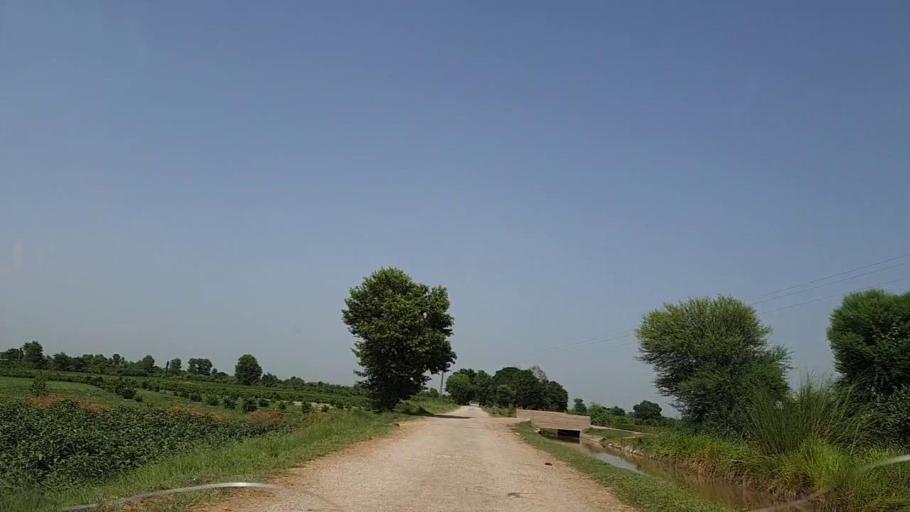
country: PK
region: Sindh
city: Kandiaro
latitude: 27.0422
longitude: 68.1610
